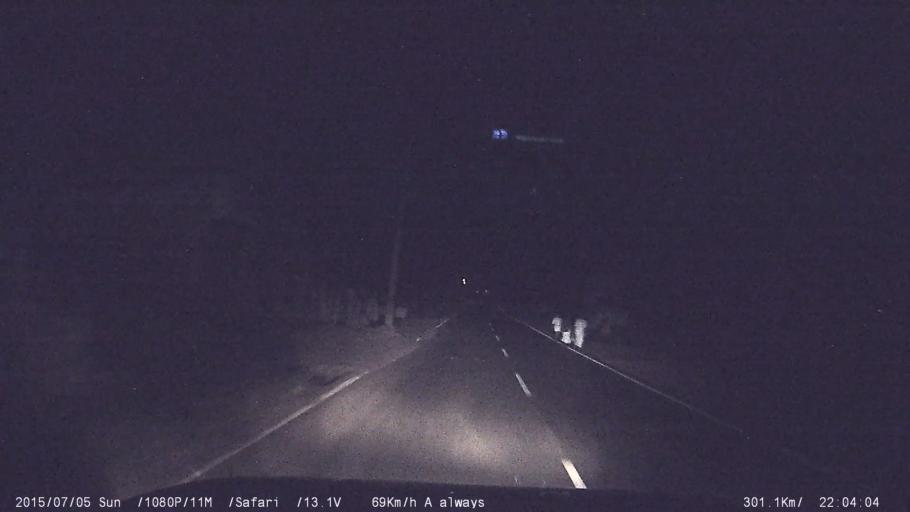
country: IN
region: Kerala
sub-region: Palakkad district
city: Mannarakkat
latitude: 10.9254
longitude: 76.5248
